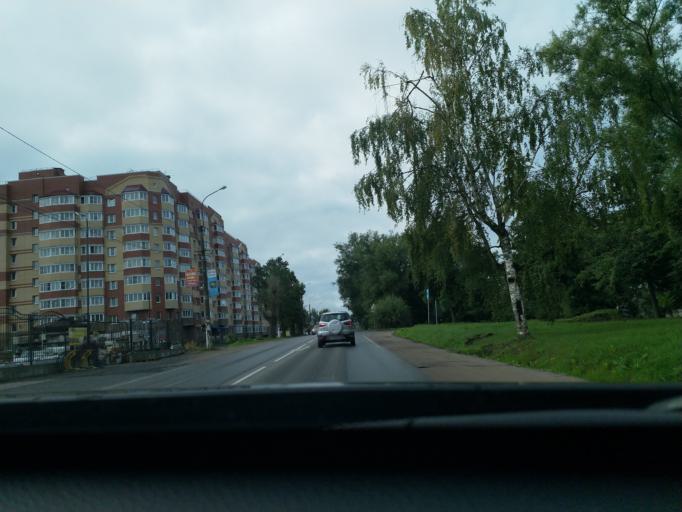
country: RU
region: Leningrad
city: Nikol'skoye
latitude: 59.6965
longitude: 30.7848
